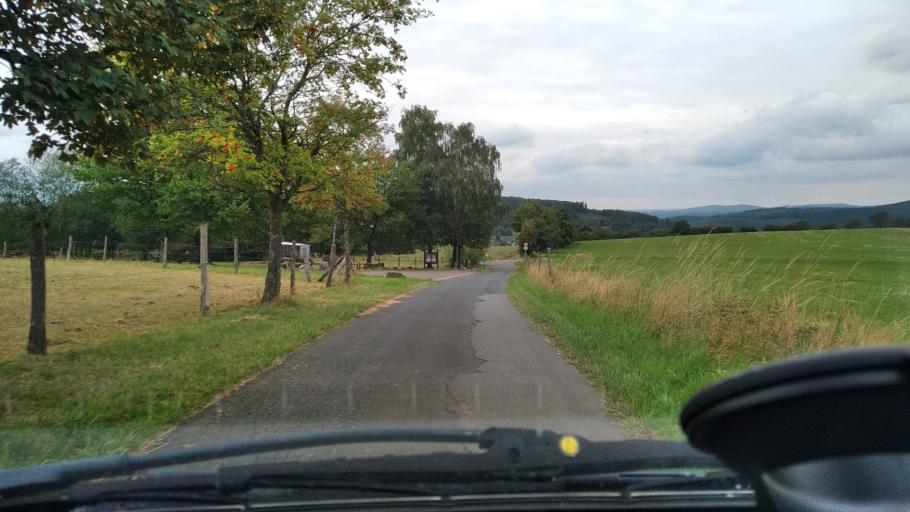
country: DE
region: Hesse
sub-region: Regierungsbezirk Giessen
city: Haiger
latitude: 50.8484
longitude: 8.2092
